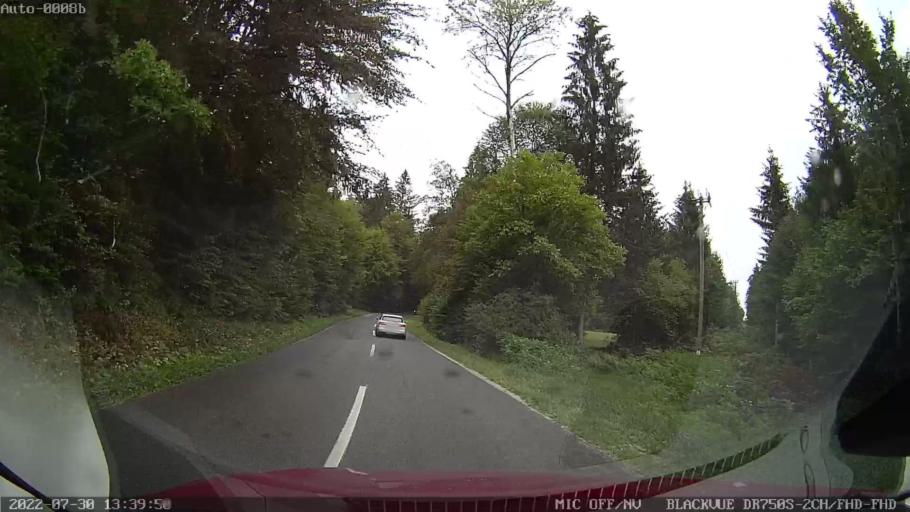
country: SI
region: Zuzemberk
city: Zuzemberk
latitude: 45.8971
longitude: 14.9058
